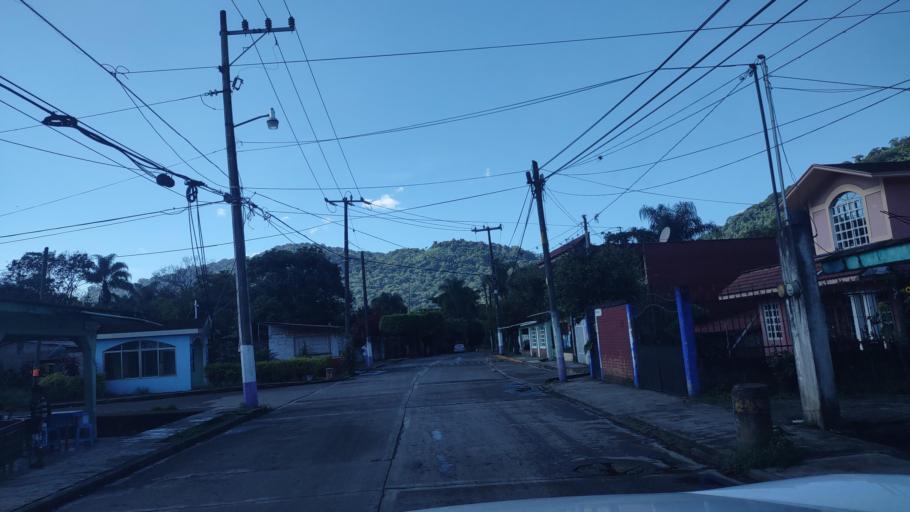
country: MX
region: Veracruz
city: Cuautlapan
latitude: 18.8670
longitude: -97.0256
